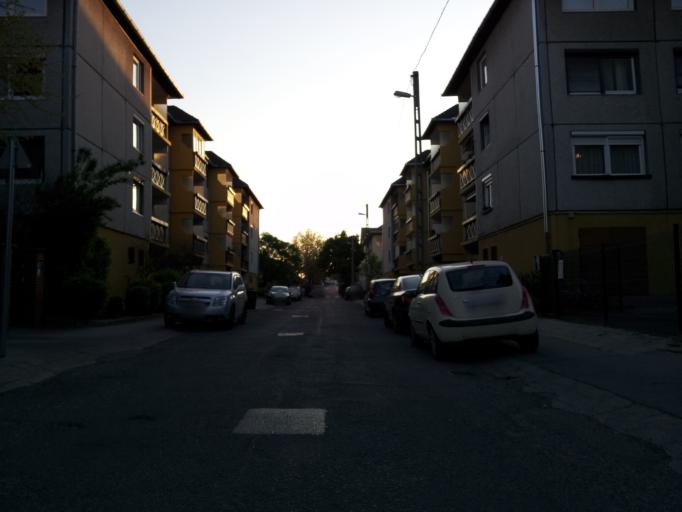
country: HU
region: Budapest
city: Budapest XIV. keruelet
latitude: 47.4963
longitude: 19.1066
